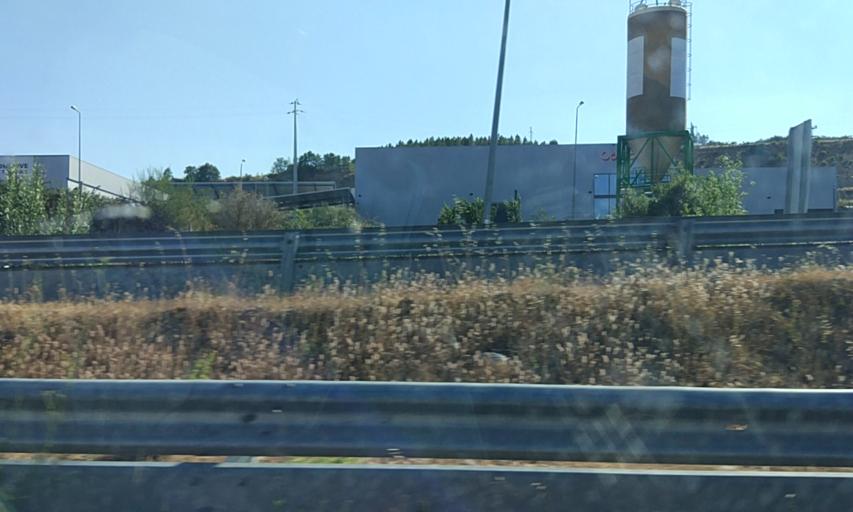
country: PT
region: Braganca
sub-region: Braganca Municipality
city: Braganca
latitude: 41.7177
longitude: -6.8076
